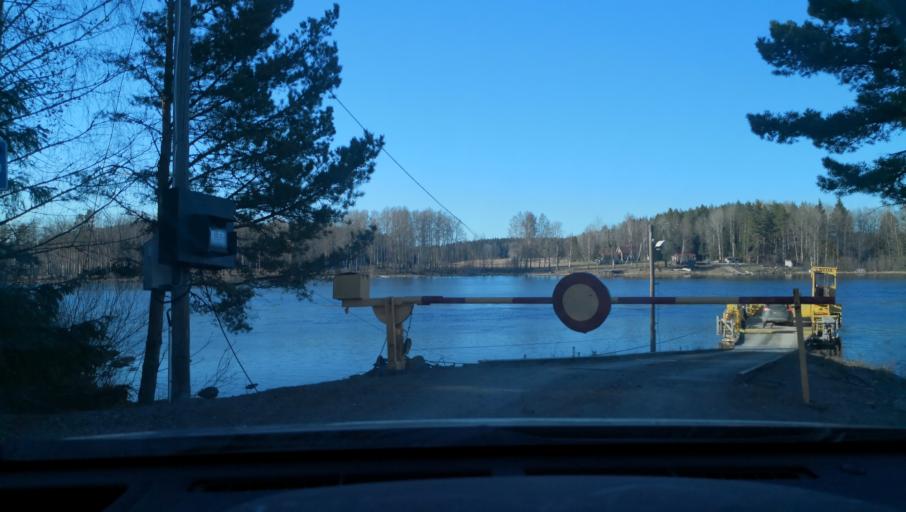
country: SE
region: Dalarna
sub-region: Avesta Kommun
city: Horndal
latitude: 60.1824
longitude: 16.6247
